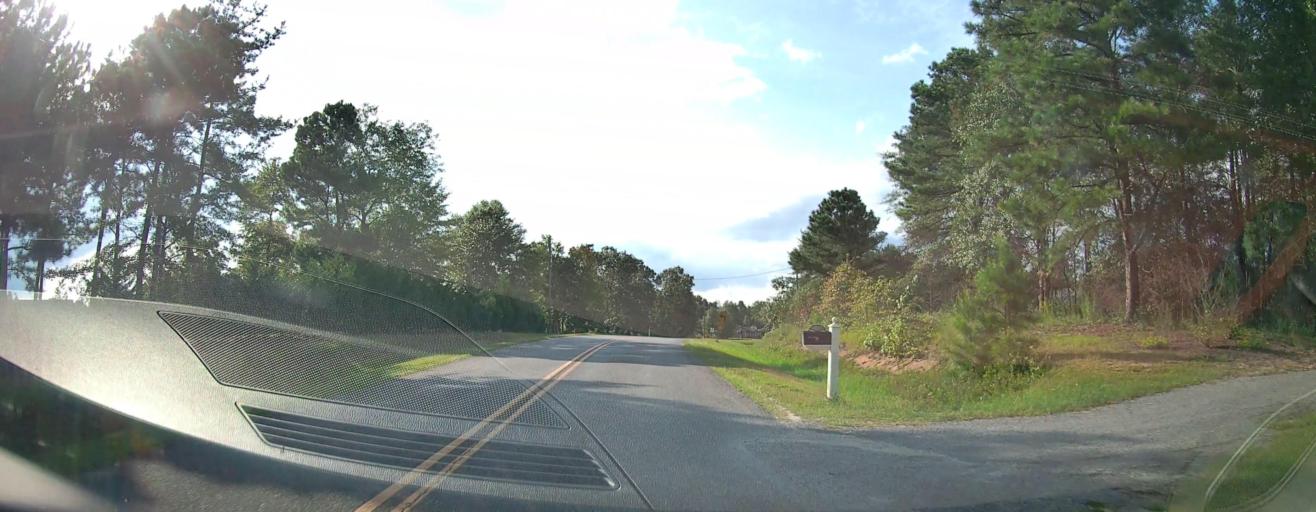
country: US
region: Georgia
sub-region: Crawford County
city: Roberta
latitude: 32.7391
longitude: -84.0140
